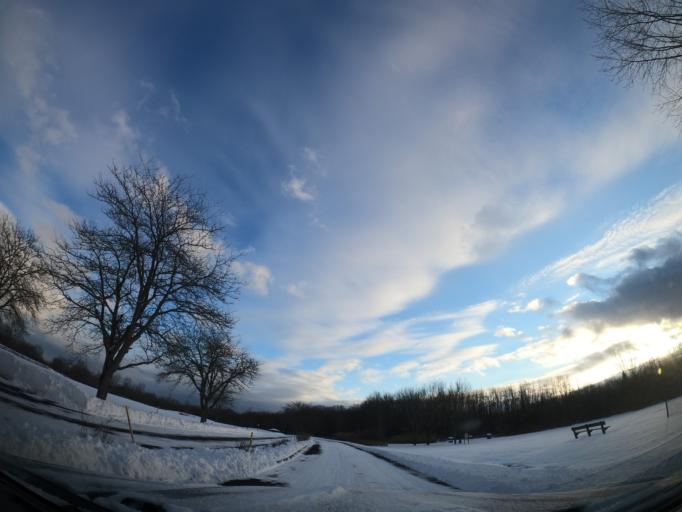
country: US
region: New York
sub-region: Onondaga County
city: Brewerton
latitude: 43.2258
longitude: -76.1106
